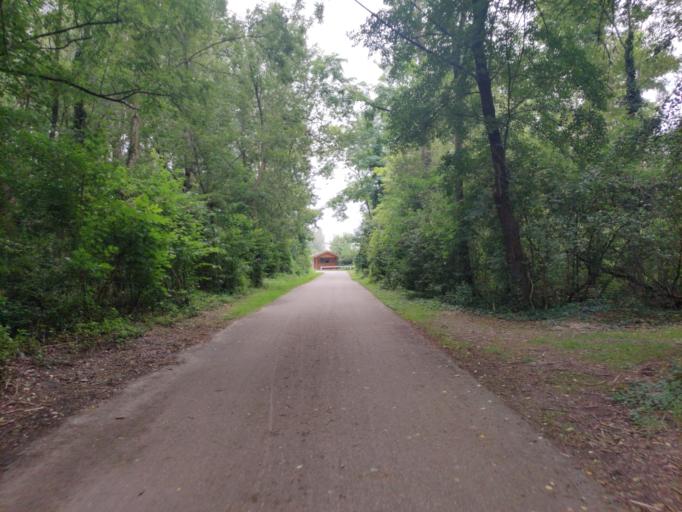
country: AT
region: Lower Austria
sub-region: Politischer Bezirk Tulln
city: Michelhausen
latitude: 48.3447
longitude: 15.9239
